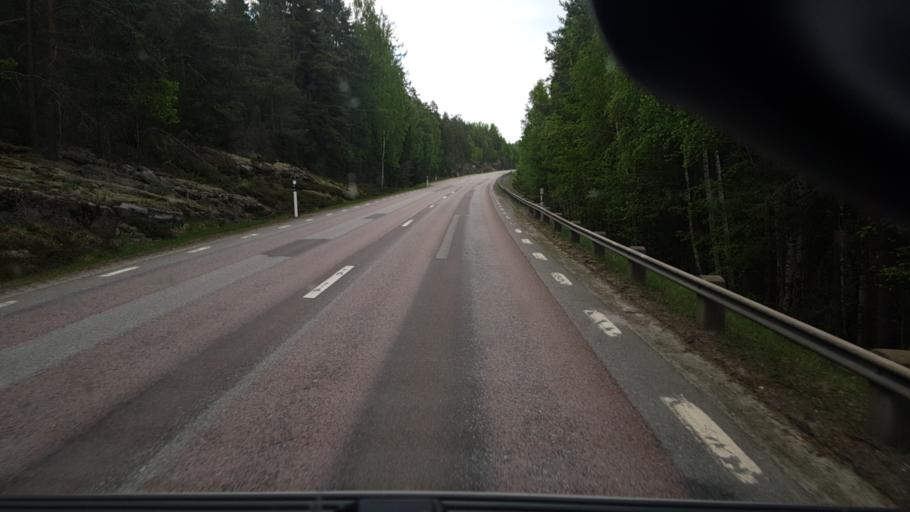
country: SE
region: Vaermland
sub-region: Arvika Kommun
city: Arvika
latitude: 59.5637
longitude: 12.7216
